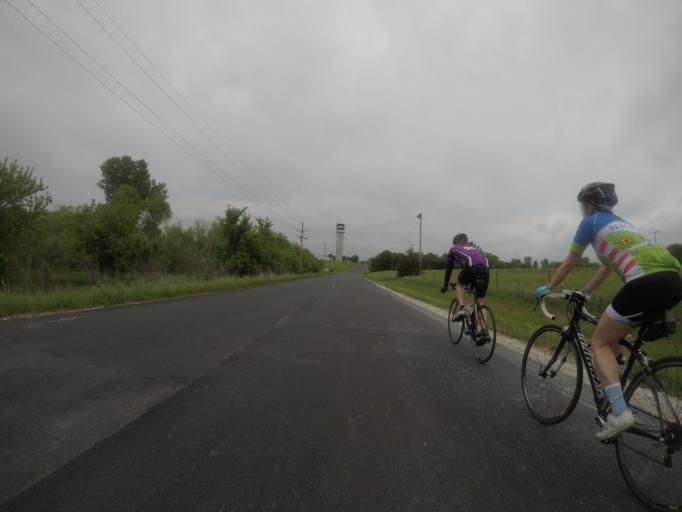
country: US
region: Kansas
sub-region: Pottawatomie County
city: Westmoreland
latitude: 39.5022
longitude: -96.1697
